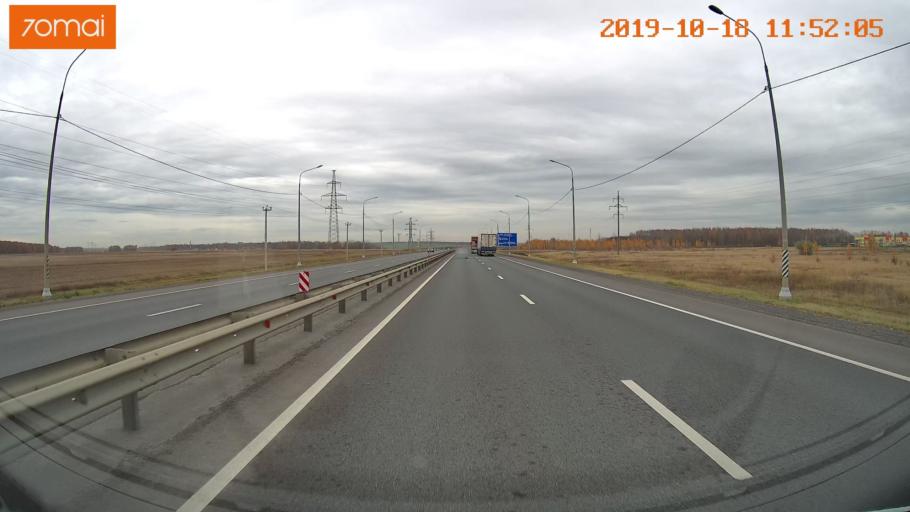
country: RU
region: Rjazan
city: Mikhaylov
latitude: 54.2507
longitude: 39.0410
